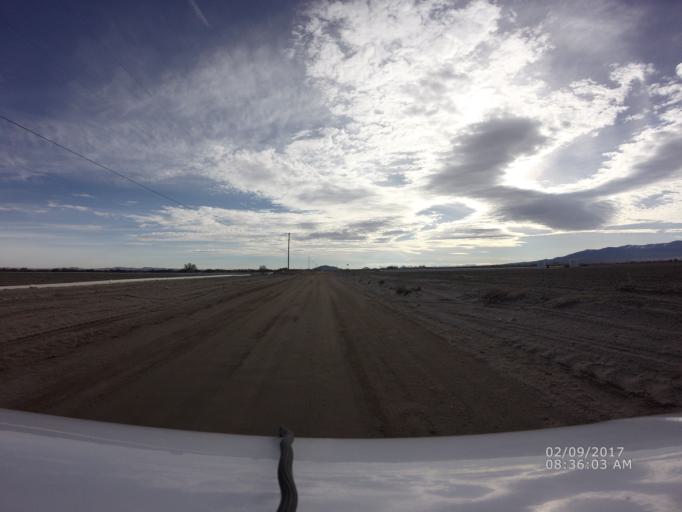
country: US
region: California
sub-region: Los Angeles County
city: Lake Los Angeles
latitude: 34.5580
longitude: -117.8452
